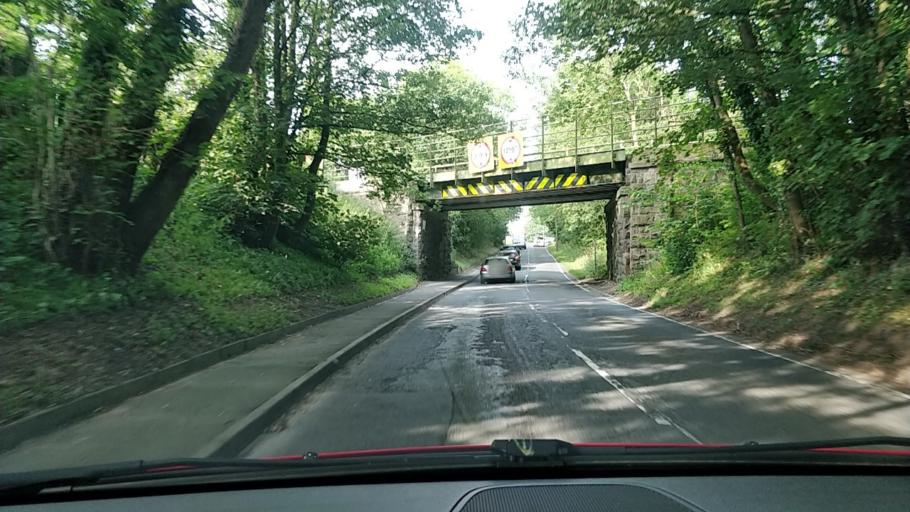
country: GB
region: Wales
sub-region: County of Flintshire
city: Penyffordd
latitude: 53.1417
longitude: -3.0554
